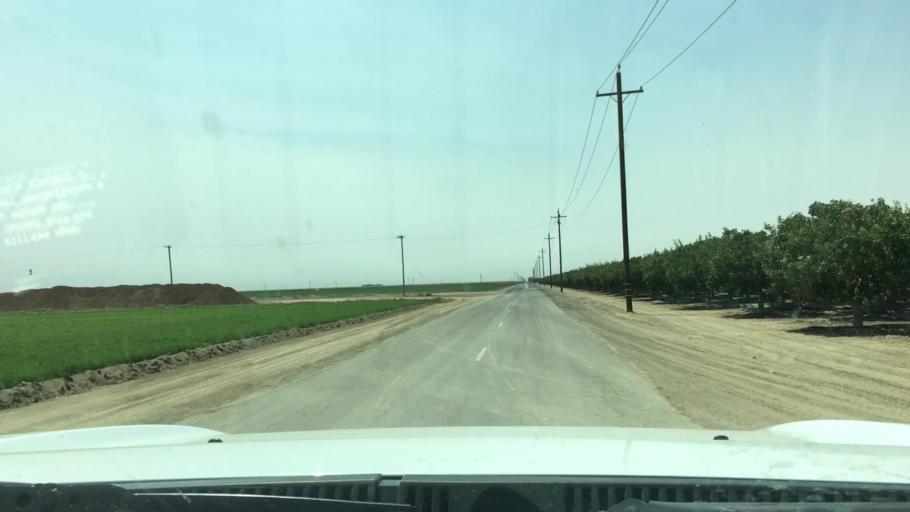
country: US
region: California
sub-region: Kern County
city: Wasco
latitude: 35.7261
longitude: -119.4371
